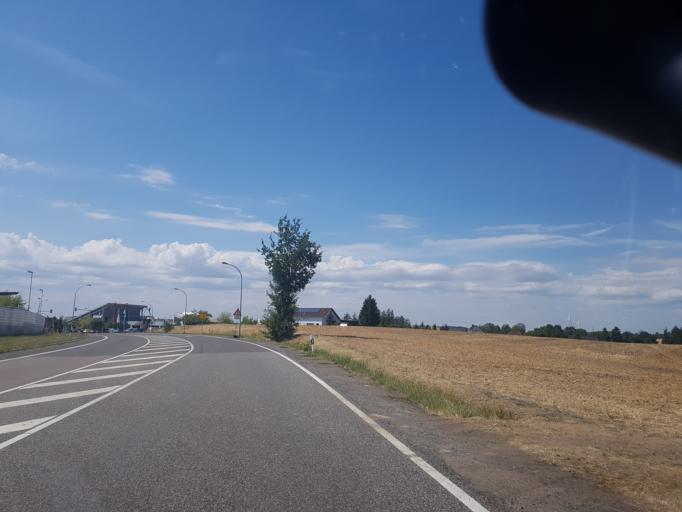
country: DE
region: Saxony
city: Waldheim
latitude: 51.0828
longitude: 12.9987
